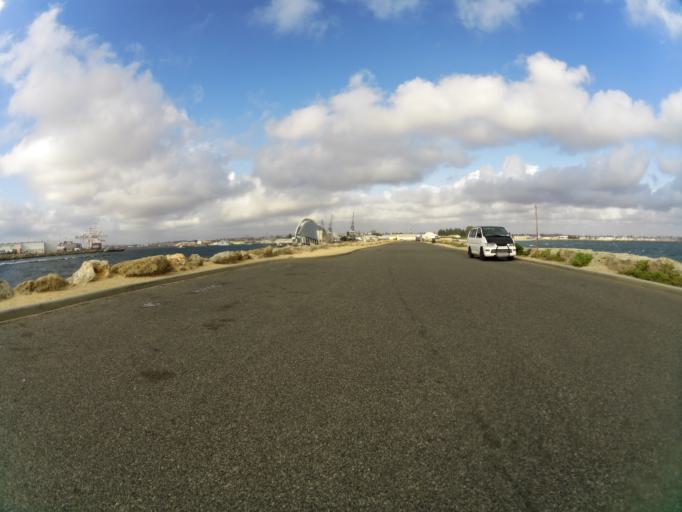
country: AU
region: Western Australia
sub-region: Fremantle
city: South Fremantle
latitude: -32.0558
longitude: 115.7337
